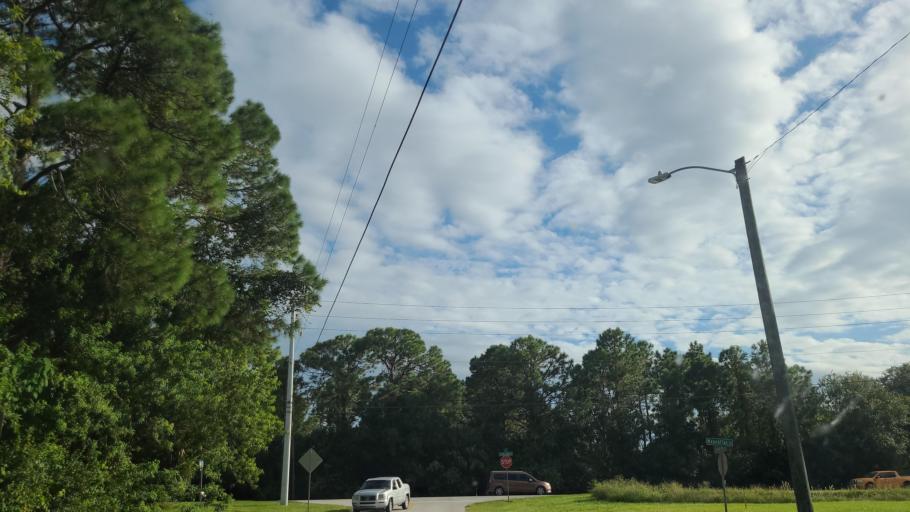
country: US
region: Florida
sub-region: Brevard County
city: June Park
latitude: 27.9996
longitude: -80.6928
